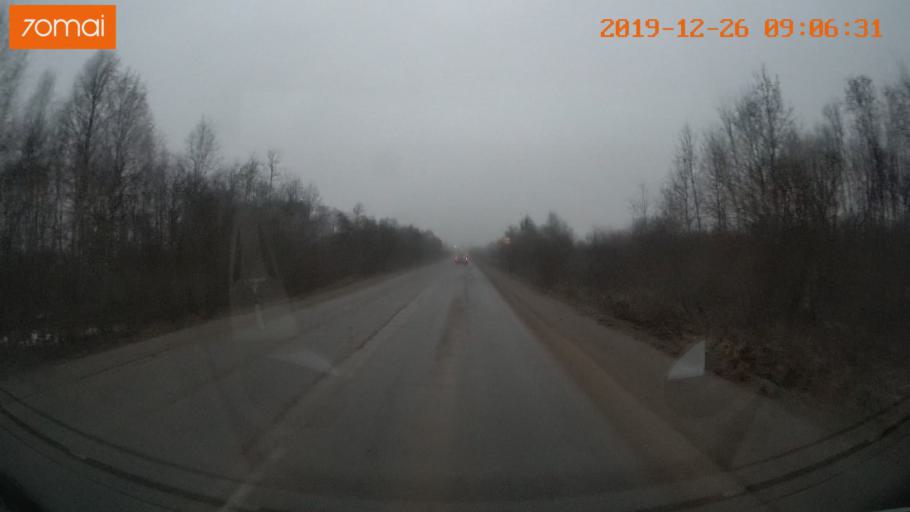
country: RU
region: Vologda
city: Gryazovets
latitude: 58.8371
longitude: 40.2528
